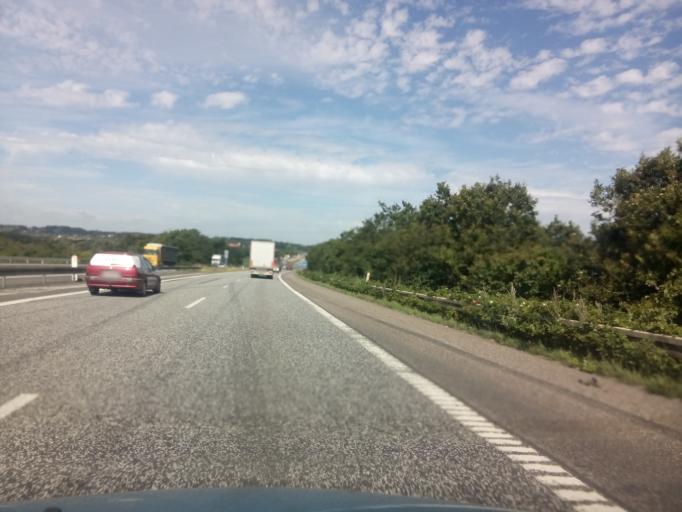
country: DK
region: Central Jutland
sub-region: Randers Kommune
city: Randers
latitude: 56.4447
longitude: 10.0072
